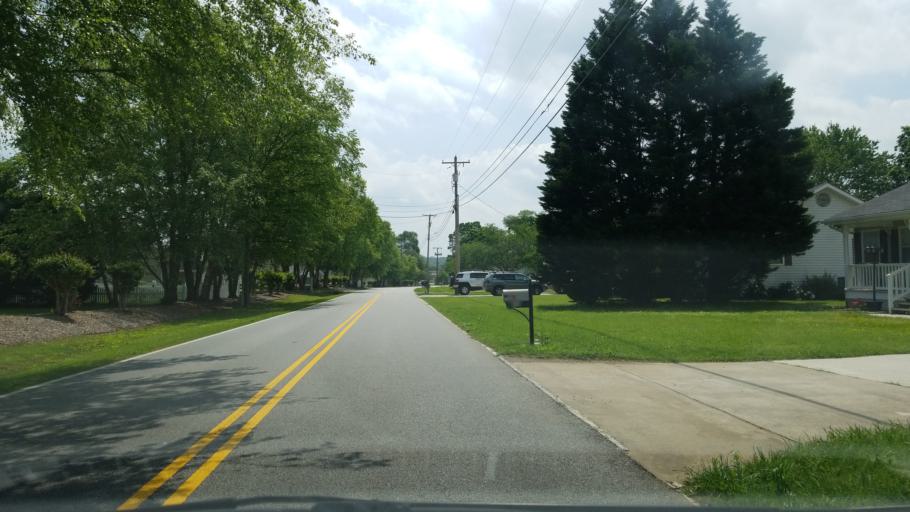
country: US
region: Tennessee
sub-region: Hamilton County
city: Soddy-Daisy
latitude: 35.2254
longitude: -85.2222
